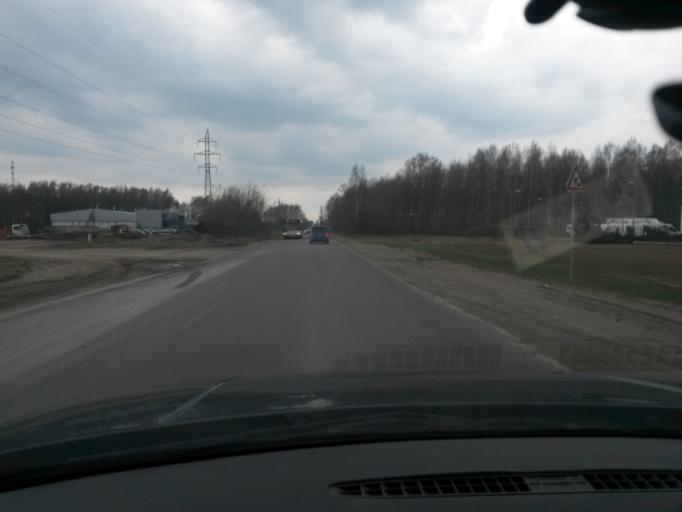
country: LV
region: Stopini
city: Ulbroka
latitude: 56.9127
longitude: 24.2279
